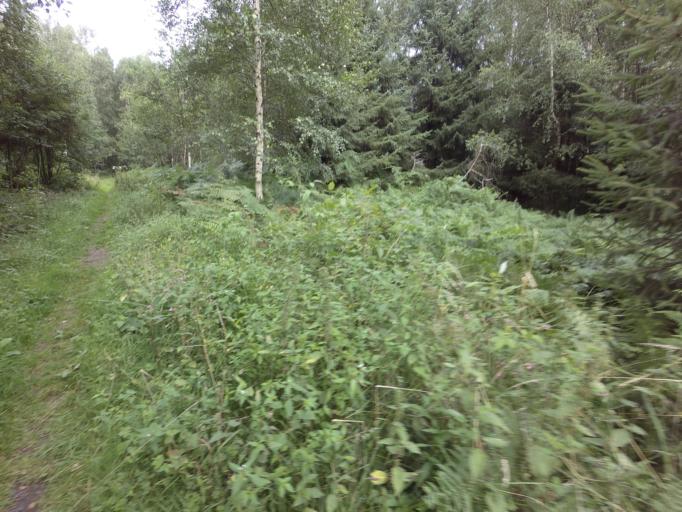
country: BE
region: Wallonia
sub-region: Province de Liege
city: Aubel
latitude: 50.7554
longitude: 5.8936
